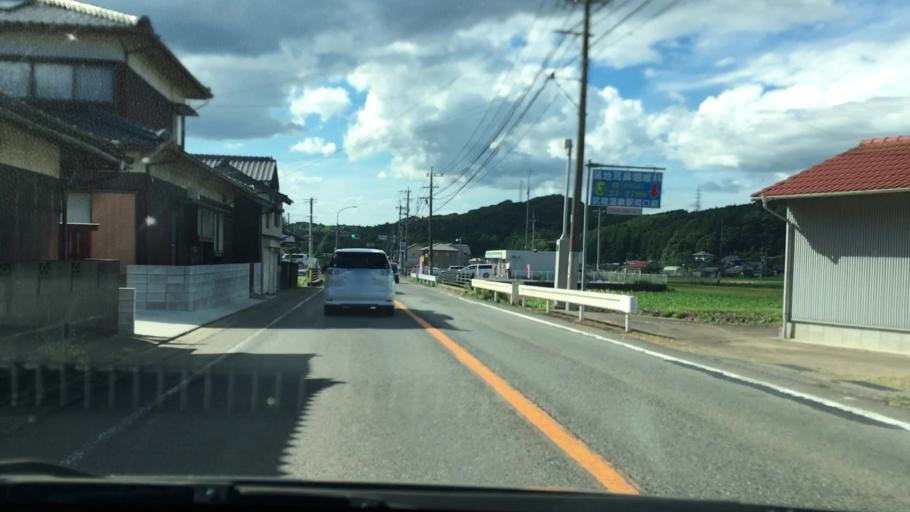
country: JP
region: Saga Prefecture
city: Takeocho-takeo
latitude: 33.1926
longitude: 129.9815
